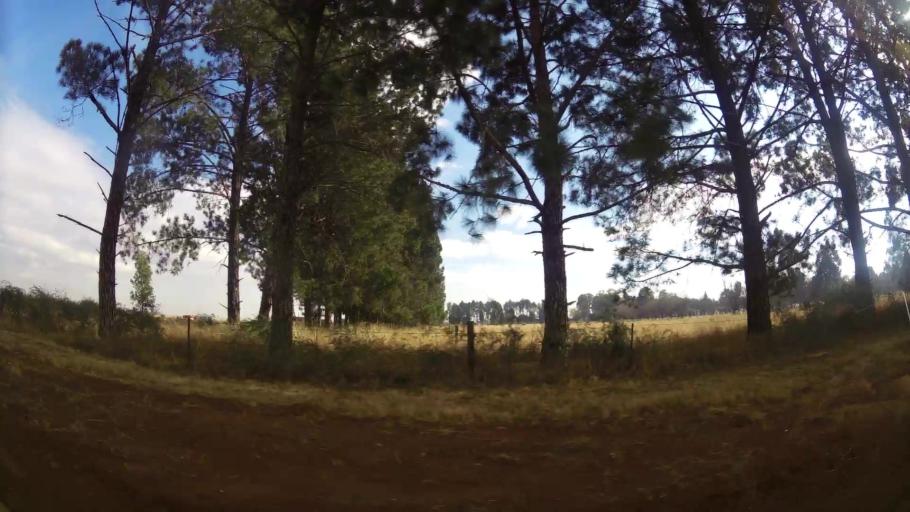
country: ZA
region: Gauteng
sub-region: Sedibeng District Municipality
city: Meyerton
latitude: -26.5535
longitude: 28.0533
